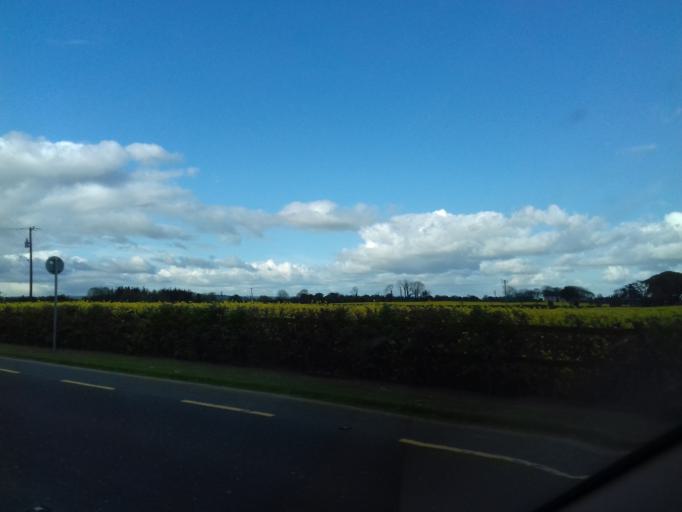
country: IE
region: Leinster
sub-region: Kilkenny
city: Kilkenny
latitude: 52.5879
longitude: -7.2409
